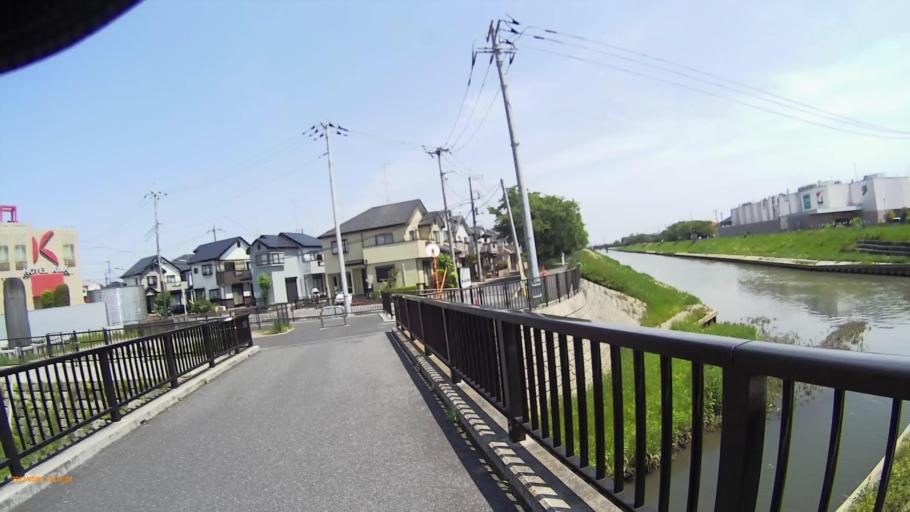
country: JP
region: Saitama
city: Kasukabe
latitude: 35.9381
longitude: 139.7773
